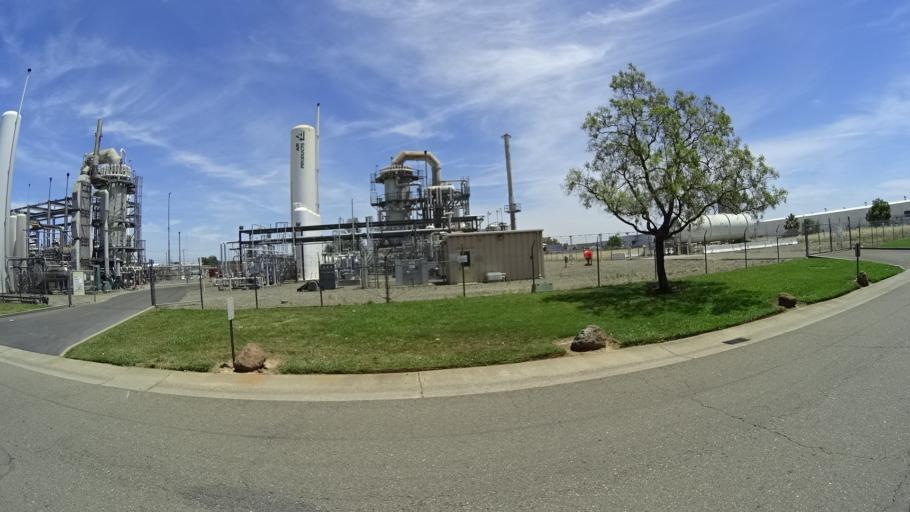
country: US
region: California
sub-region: Sacramento County
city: Florin
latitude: 38.5289
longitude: -121.3992
